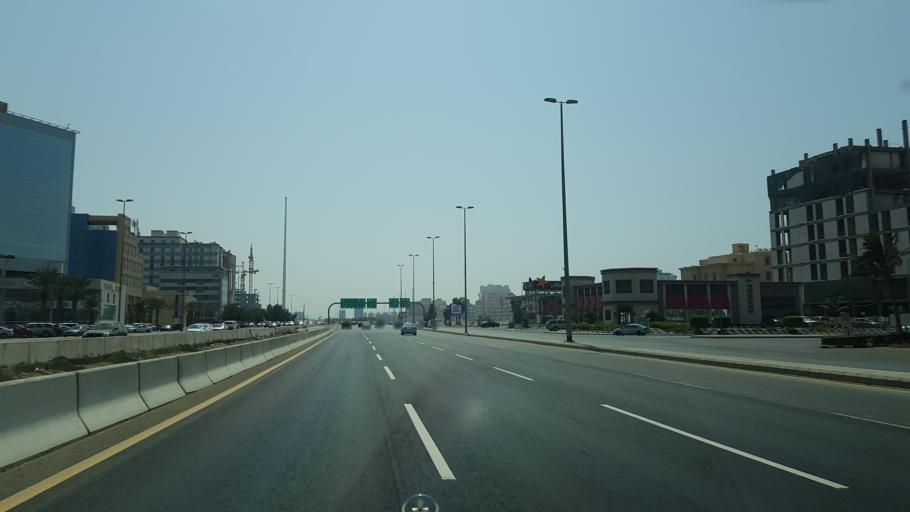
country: SA
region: Makkah
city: Jeddah
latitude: 21.5163
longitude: 39.1662
